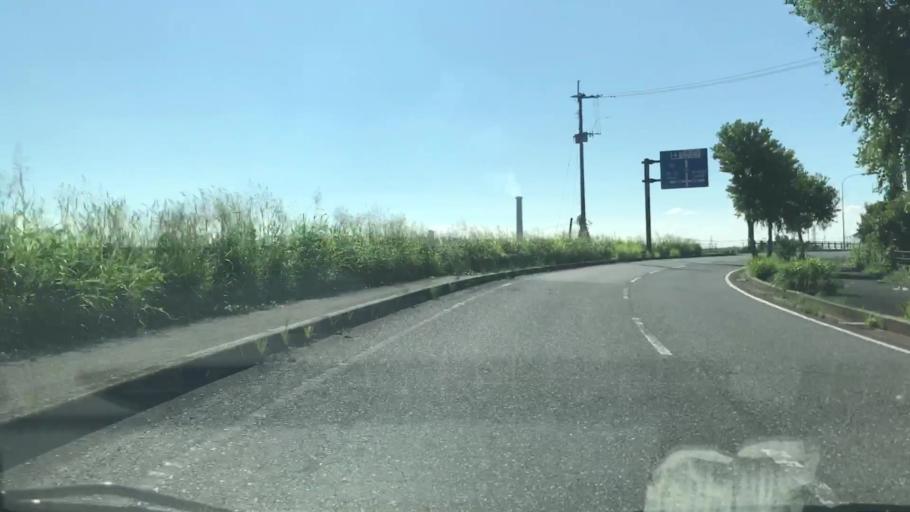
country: JP
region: Saga Prefecture
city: Okawa
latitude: 33.2277
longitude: 130.3717
